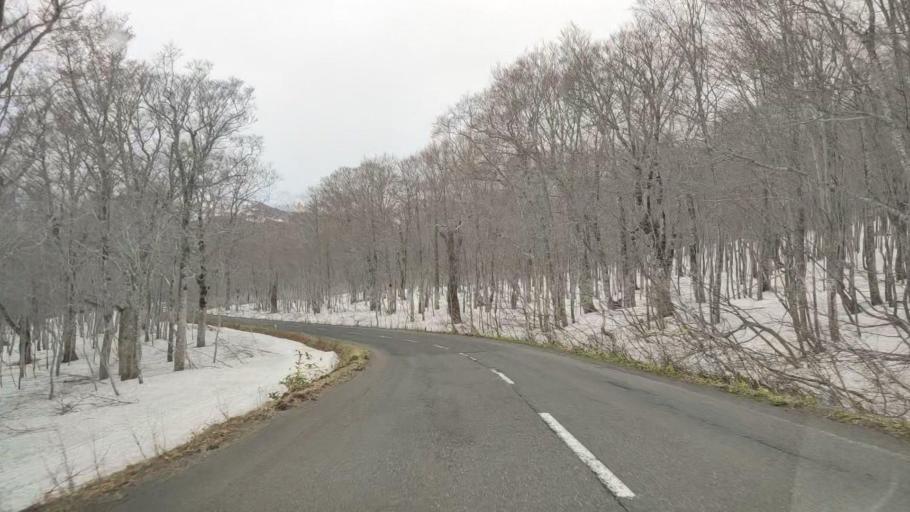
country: JP
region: Aomori
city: Aomori Shi
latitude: 40.6386
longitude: 140.9316
